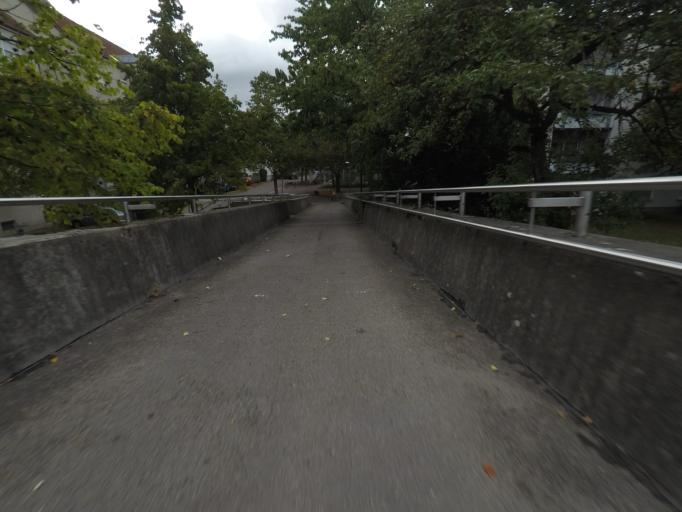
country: DE
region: Baden-Wuerttemberg
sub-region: Regierungsbezirk Stuttgart
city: Steinenbronn
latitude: 48.7254
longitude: 9.1098
